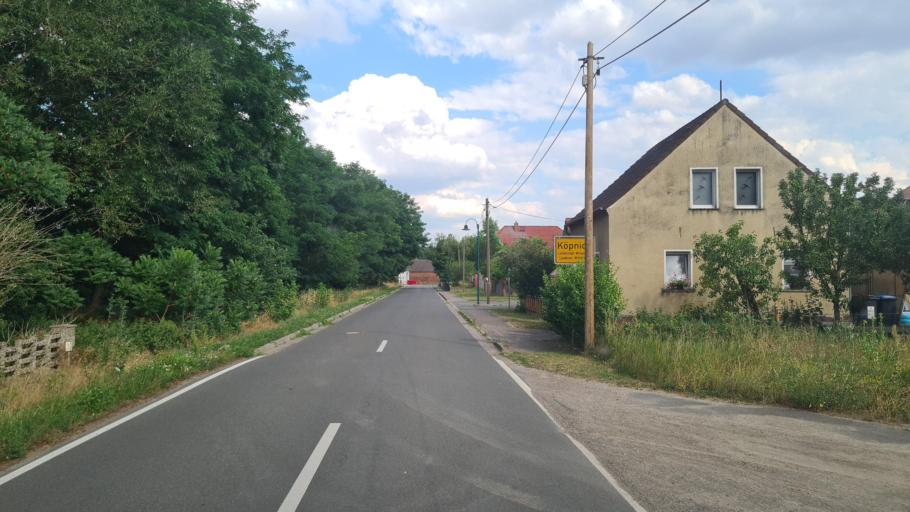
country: DE
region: Saxony-Anhalt
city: Kropstadt
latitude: 51.9407
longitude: 12.7076
